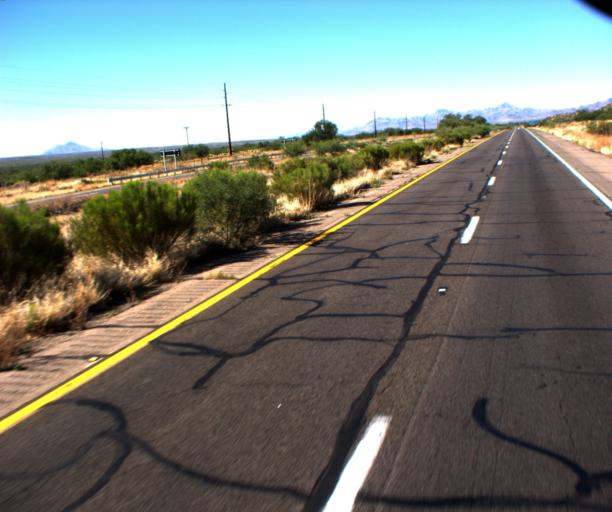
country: US
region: Arizona
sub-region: Pima County
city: Arivaca Junction
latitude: 31.7591
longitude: -111.0395
